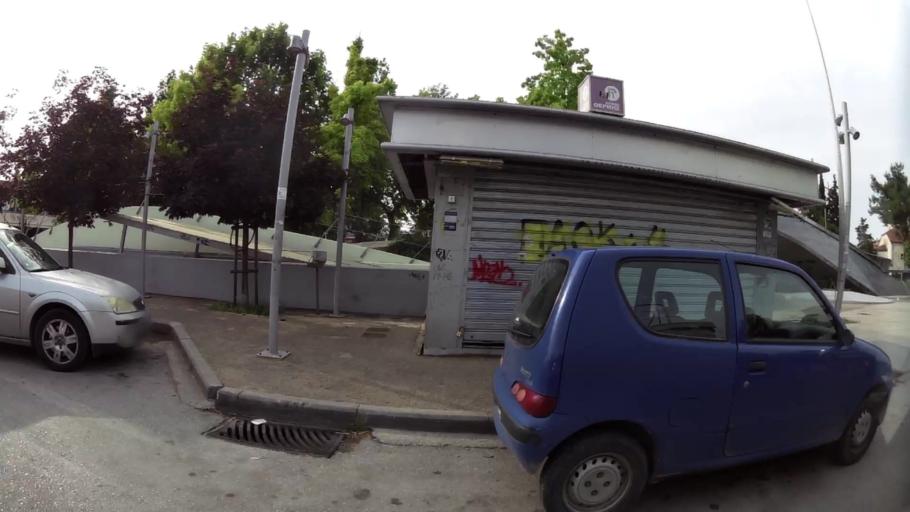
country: GR
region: Central Macedonia
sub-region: Nomos Thessalonikis
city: Thermi
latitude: 40.5473
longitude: 23.0194
